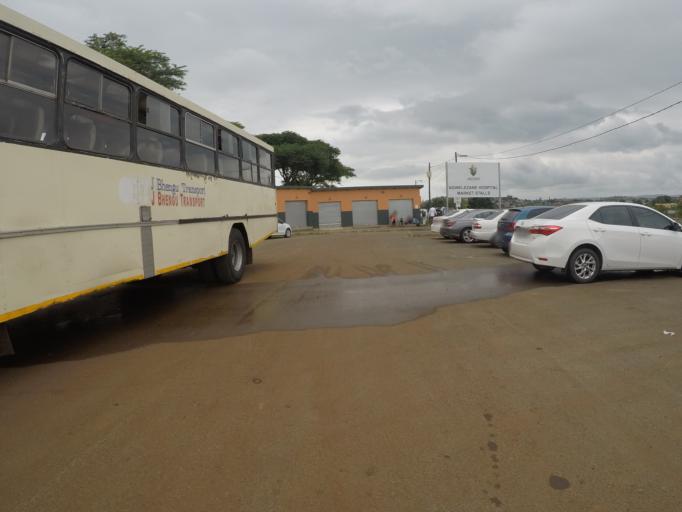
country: ZA
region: KwaZulu-Natal
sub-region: uThungulu District Municipality
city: Empangeni
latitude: -28.7769
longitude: 31.8652
